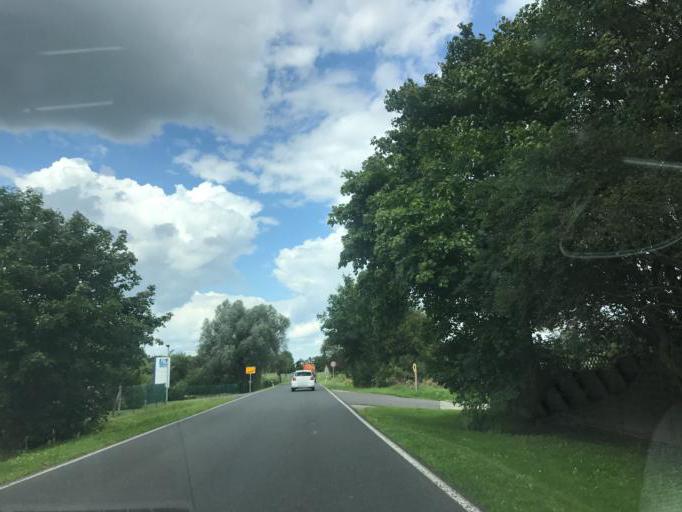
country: DE
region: Brandenburg
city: Gransee
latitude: 53.0081
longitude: 13.1422
